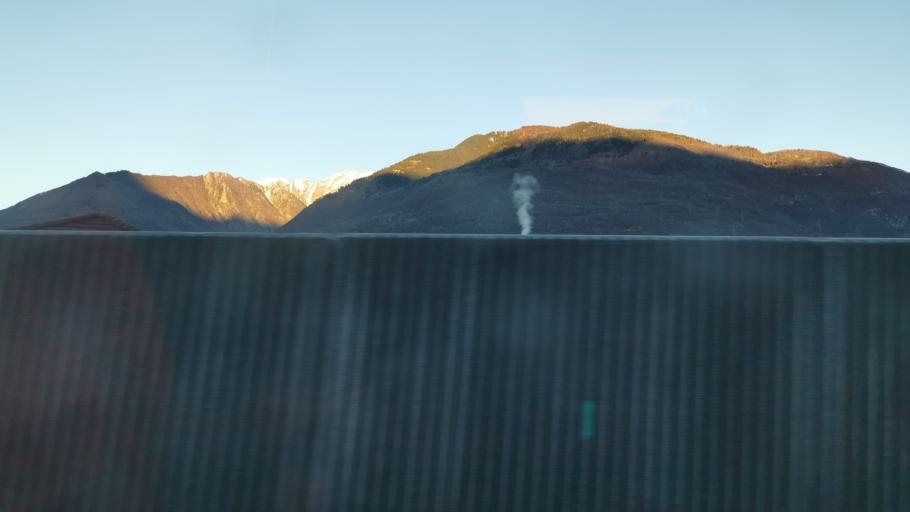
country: CH
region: Ticino
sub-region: Bellinzona District
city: Bellinzona
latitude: 46.1832
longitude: 9.0170
